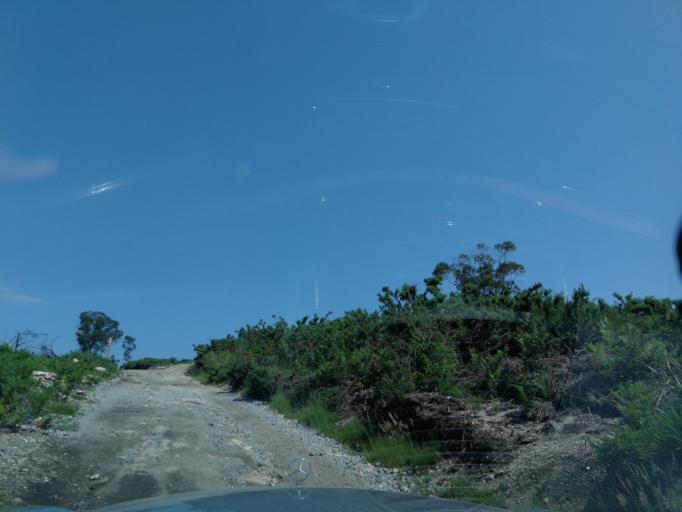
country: PT
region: Braga
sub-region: Povoa de Lanhoso
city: Povoa de Lanhoso
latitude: 41.5641
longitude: -8.3405
